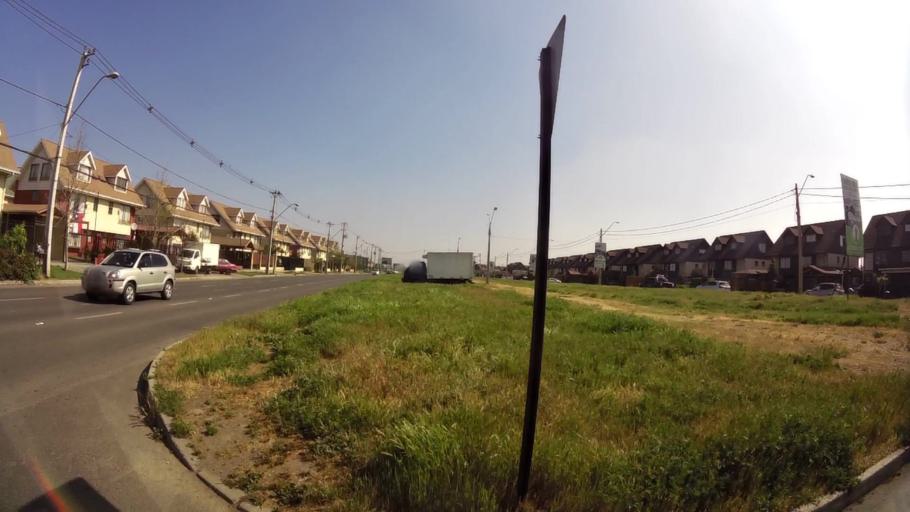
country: CL
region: Santiago Metropolitan
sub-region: Provincia de Santiago
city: Lo Prado
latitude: -33.4810
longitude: -70.7607
